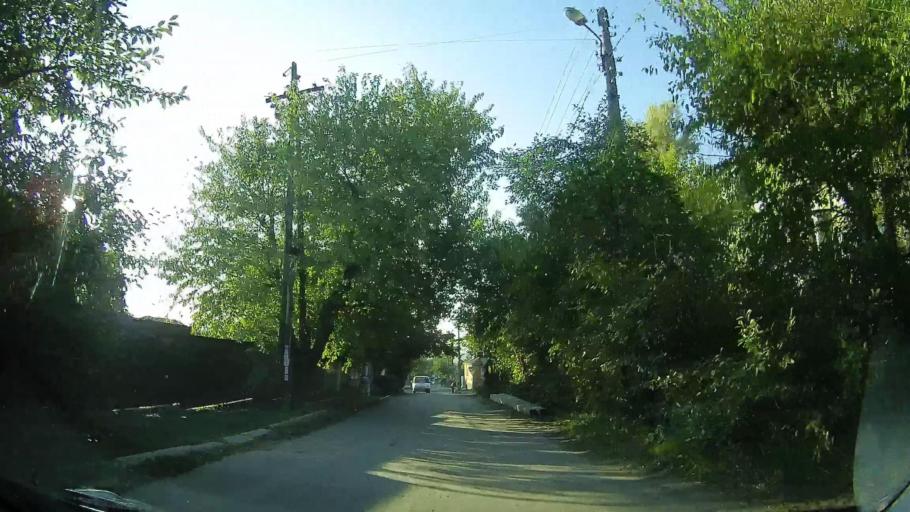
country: RU
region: Rostov
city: Severnyy
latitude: 47.2687
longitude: 39.6730
